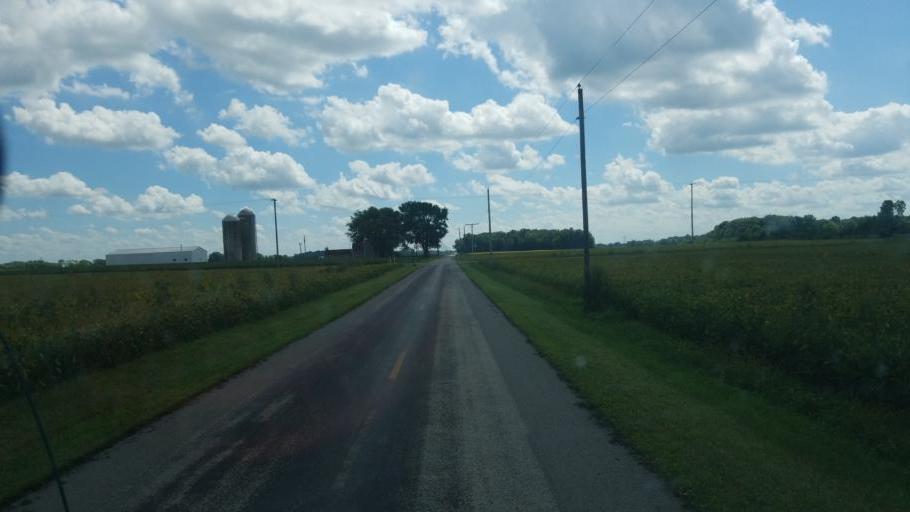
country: US
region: Ohio
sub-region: Marion County
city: Prospect
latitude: 40.4850
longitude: -83.1664
